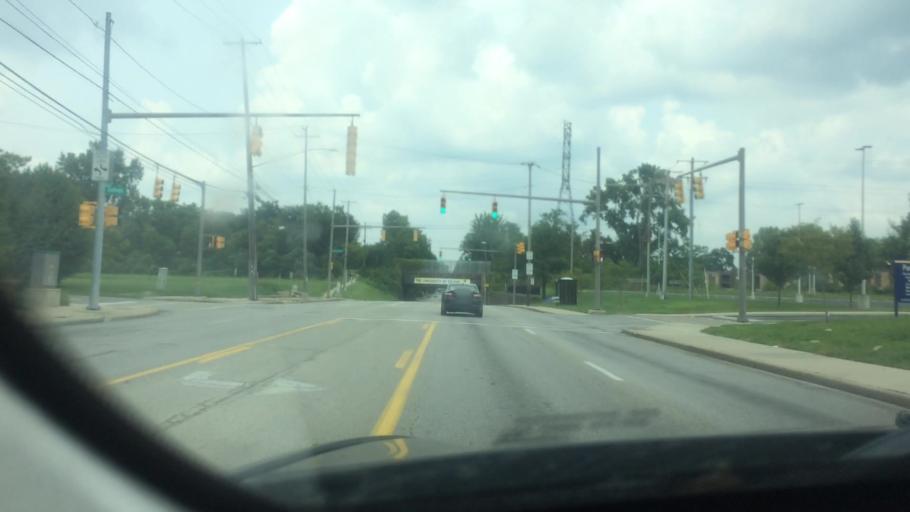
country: US
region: Ohio
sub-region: Lucas County
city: Ottawa Hills
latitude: 41.6548
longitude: -83.6219
